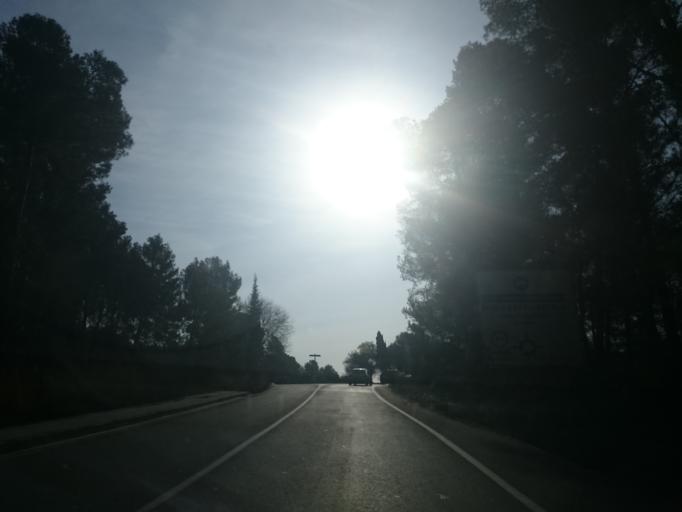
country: ES
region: Catalonia
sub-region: Provincia de Barcelona
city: Gava
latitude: 41.3014
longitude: 1.9901
